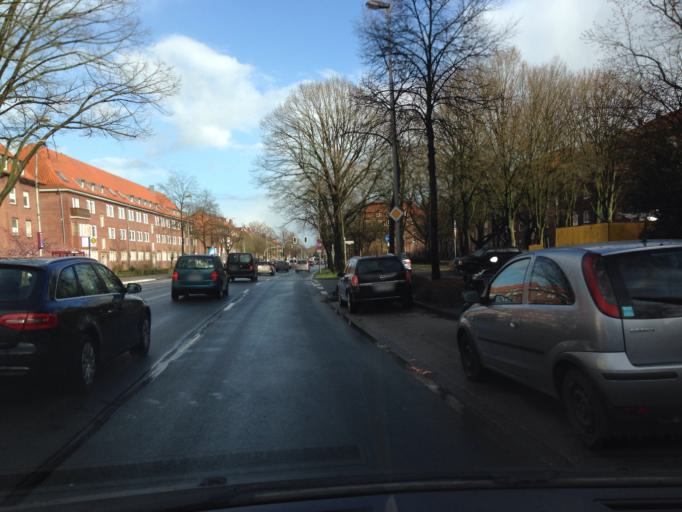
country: DE
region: North Rhine-Westphalia
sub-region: Regierungsbezirk Munster
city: Muenster
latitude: 51.9744
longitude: 7.6265
